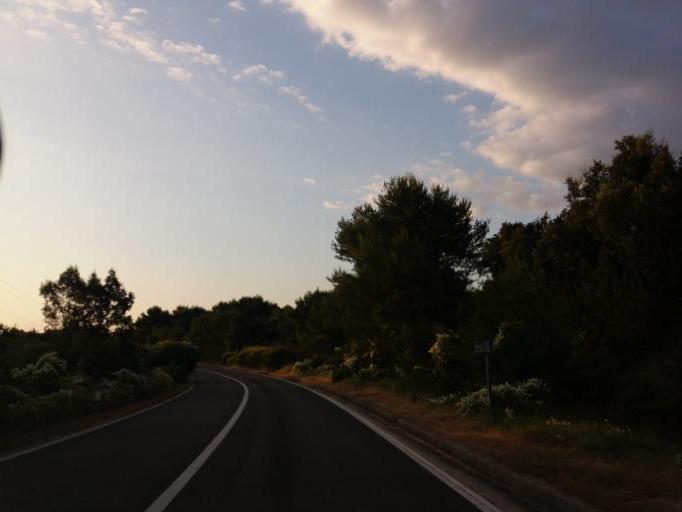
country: HR
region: Zadarska
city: Ugljan
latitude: 44.1348
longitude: 14.8553
